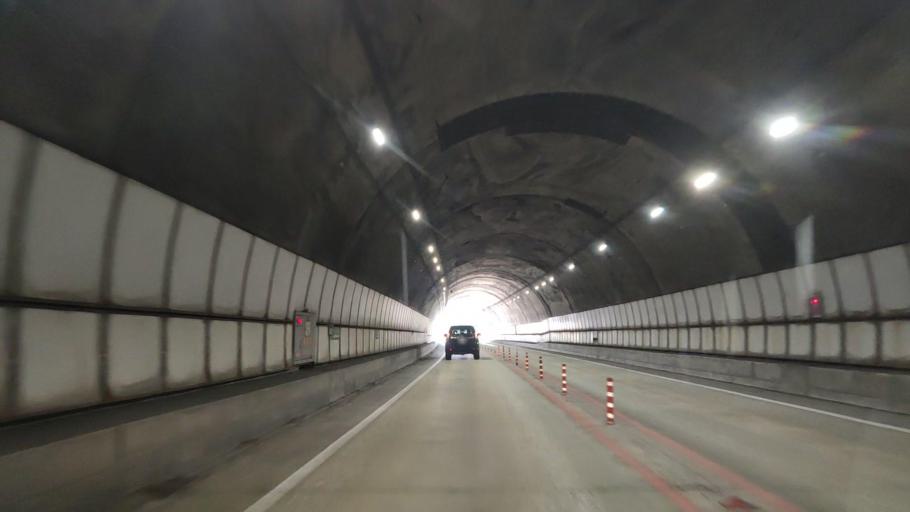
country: JP
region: Yamagata
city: Shinjo
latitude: 38.6787
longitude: 140.3193
